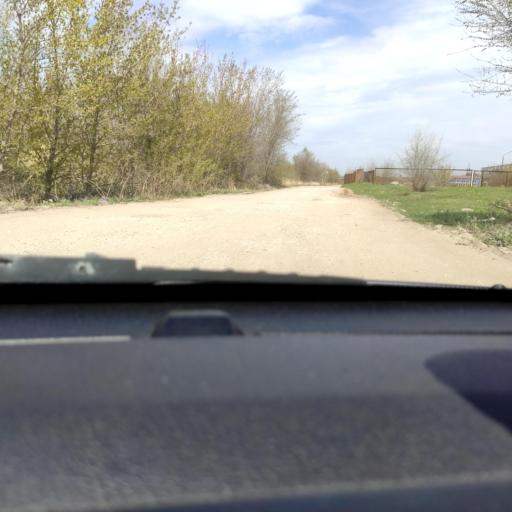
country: RU
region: Samara
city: Podstepki
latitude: 53.5762
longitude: 49.2279
